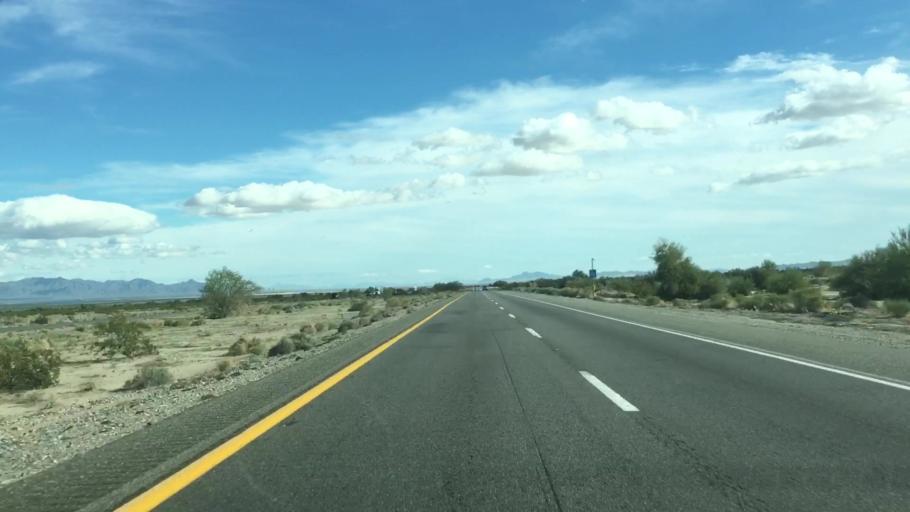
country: US
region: California
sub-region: Riverside County
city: Mesa Verde
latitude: 33.6603
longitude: -115.1691
